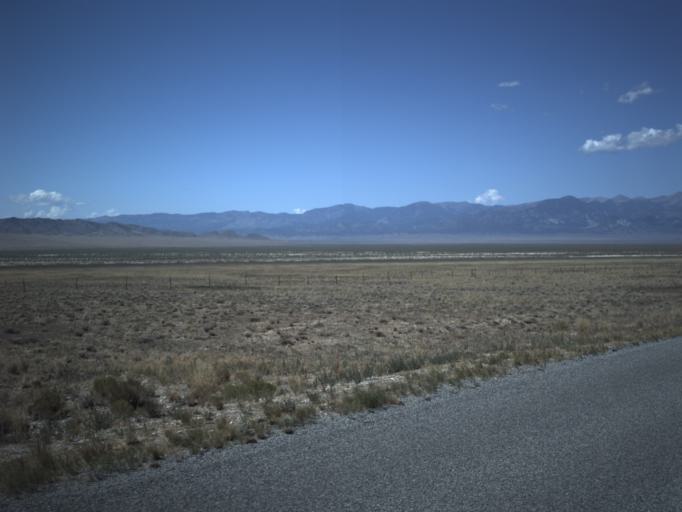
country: US
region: Nevada
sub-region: White Pine County
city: McGill
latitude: 39.0411
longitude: -113.8401
